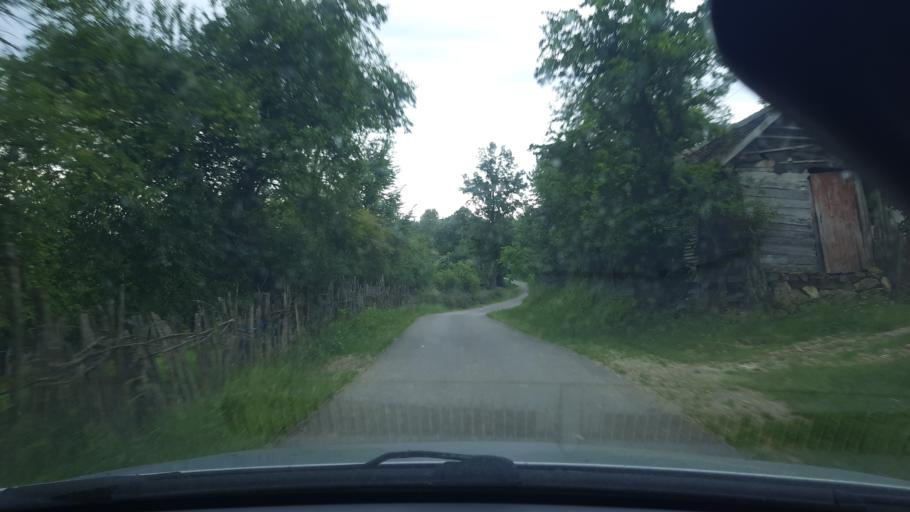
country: RS
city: Jarebice
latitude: 44.5084
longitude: 19.4746
